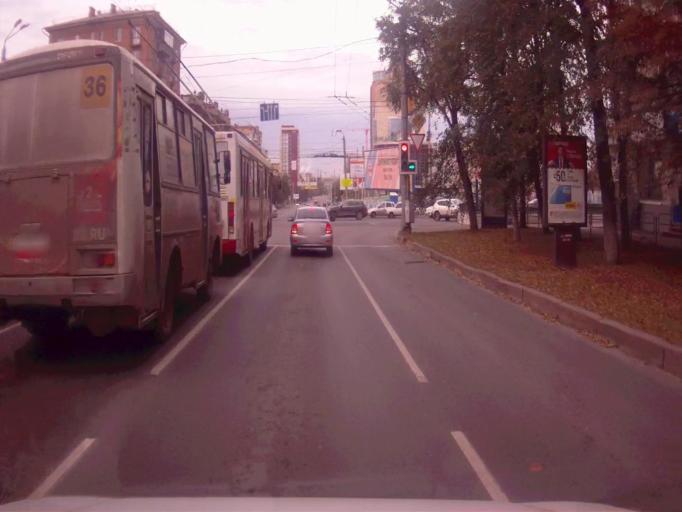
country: RU
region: Chelyabinsk
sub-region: Gorod Chelyabinsk
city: Chelyabinsk
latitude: 55.1601
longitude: 61.4116
